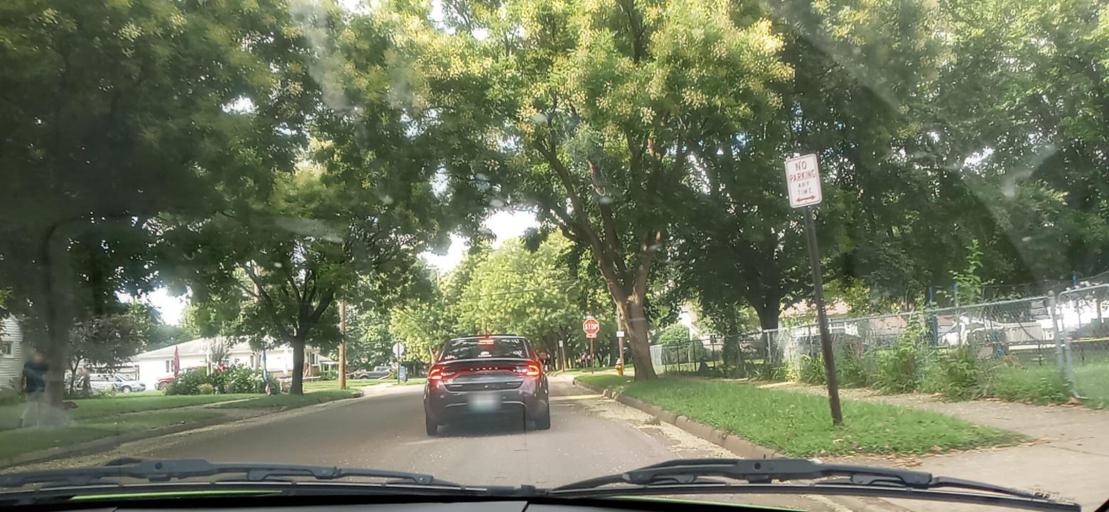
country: US
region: Ohio
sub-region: Summit County
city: Portage Lakes
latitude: 41.0260
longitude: -81.5634
